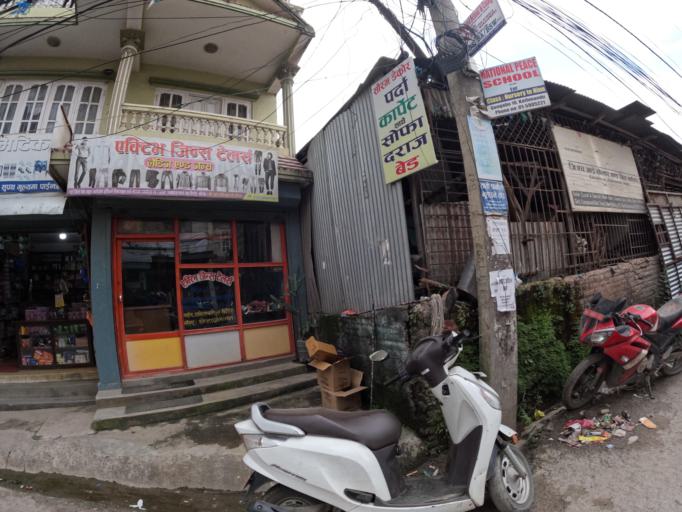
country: NP
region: Central Region
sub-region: Bagmati Zone
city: Kathmandu
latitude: 27.7368
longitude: 85.3178
